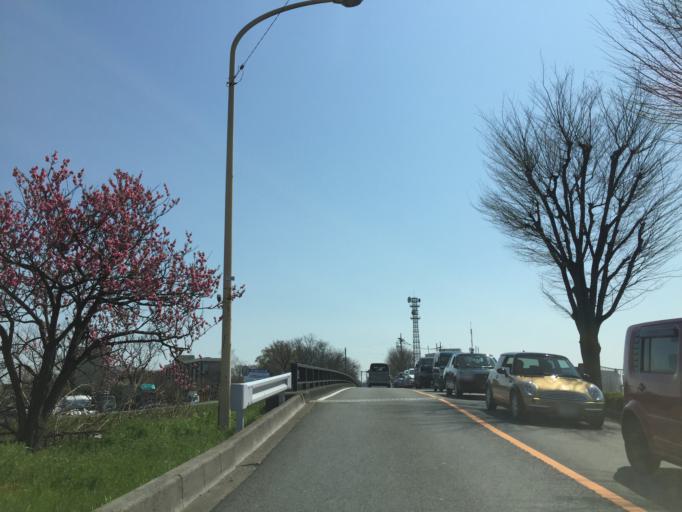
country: JP
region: Saitama
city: Shiki
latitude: 35.8613
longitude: 139.6022
